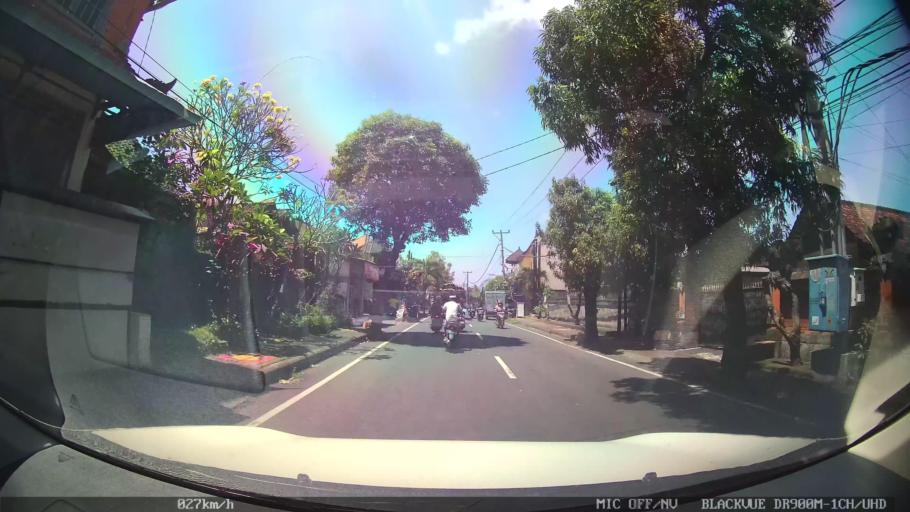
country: ID
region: Bali
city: Banjar Sedang
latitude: -8.5662
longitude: 115.3032
